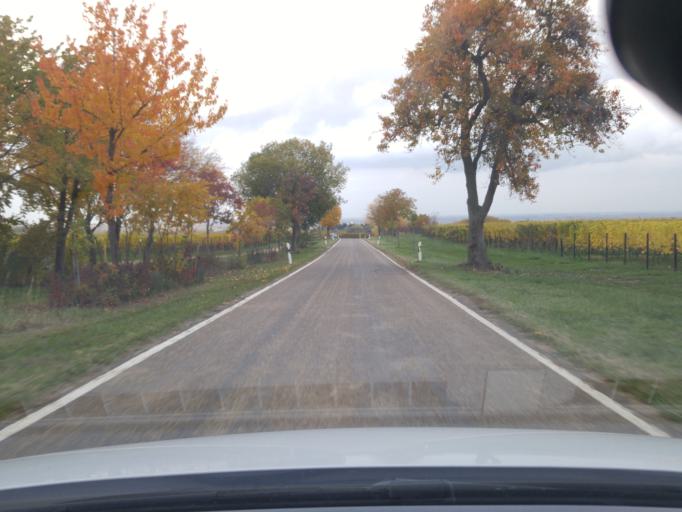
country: DE
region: Rheinland-Pfalz
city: Gleisweiler
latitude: 49.2330
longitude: 8.0746
